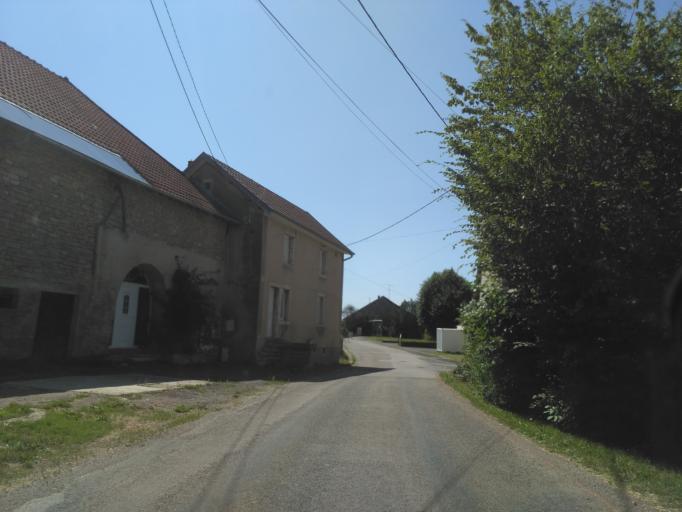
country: FR
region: Franche-Comte
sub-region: Departement du Doubs
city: Clerval
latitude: 47.4952
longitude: 6.5324
